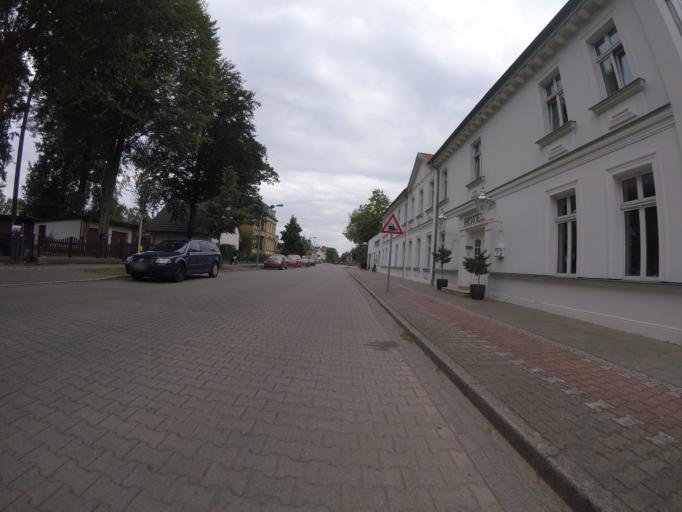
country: DE
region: Brandenburg
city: Birkenwerder
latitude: 52.7142
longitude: 13.2788
